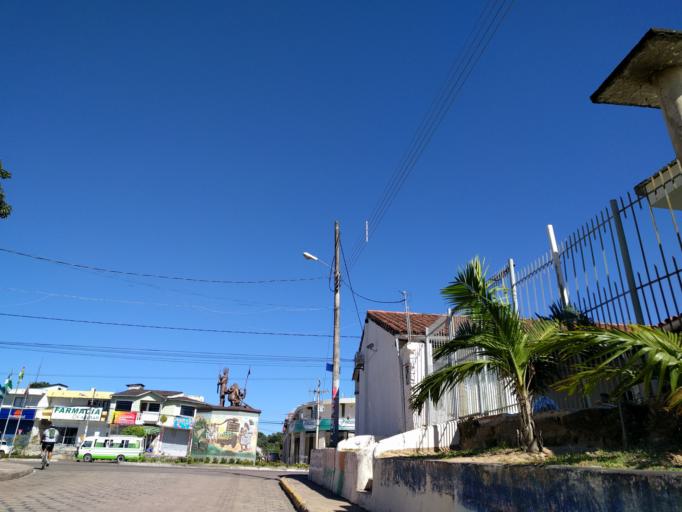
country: BO
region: Santa Cruz
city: Santa Rita
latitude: -17.8928
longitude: -63.3302
